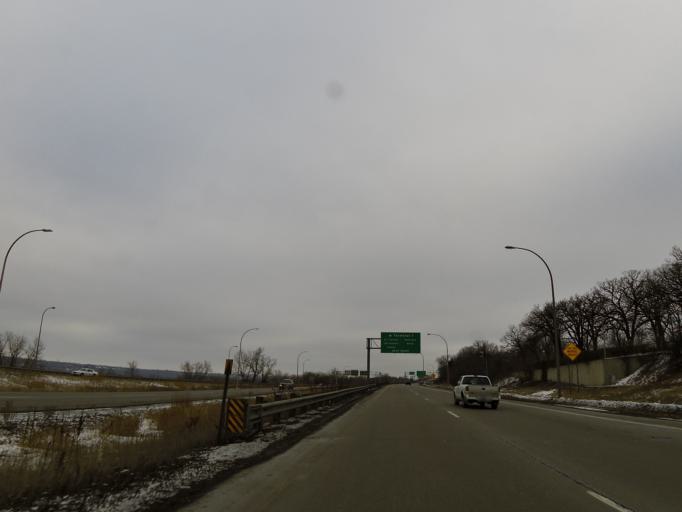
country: US
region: Minnesota
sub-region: Dakota County
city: Mendota Heights
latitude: 44.8877
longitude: -93.1871
